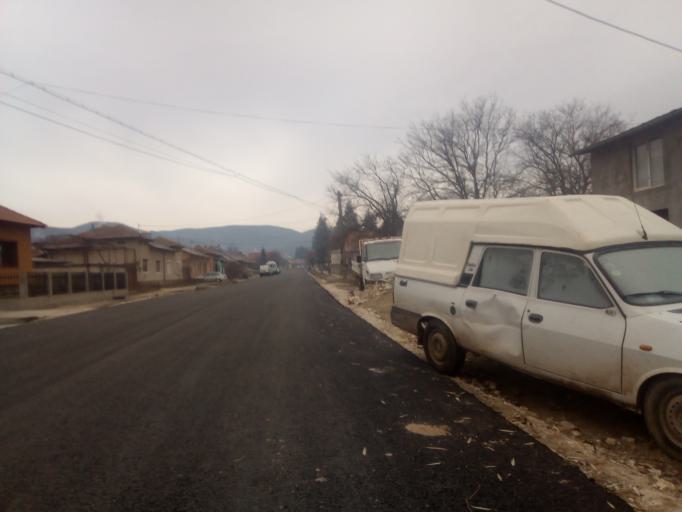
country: RO
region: Mehedinti
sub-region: Comuna Eselnita
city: Eselnita
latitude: 44.6972
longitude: 22.3651
